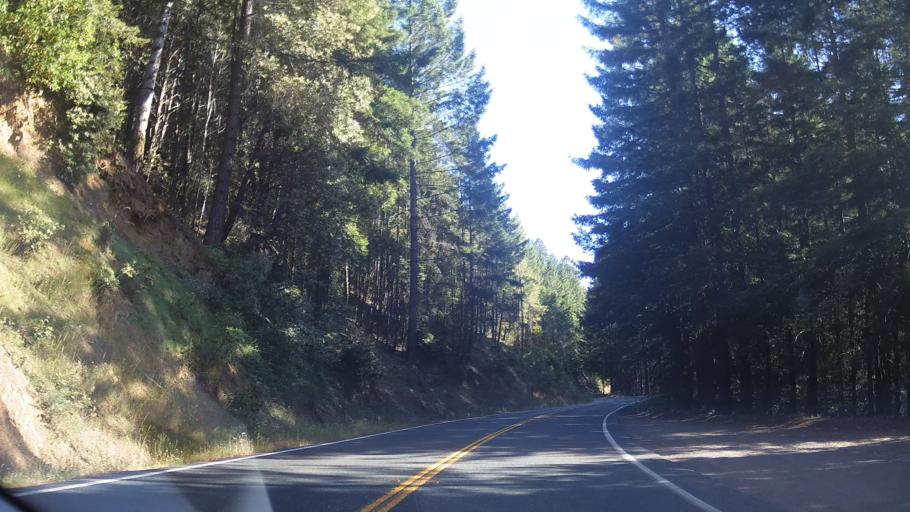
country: US
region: California
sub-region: Mendocino County
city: Brooktrails
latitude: 39.3886
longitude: -123.4675
